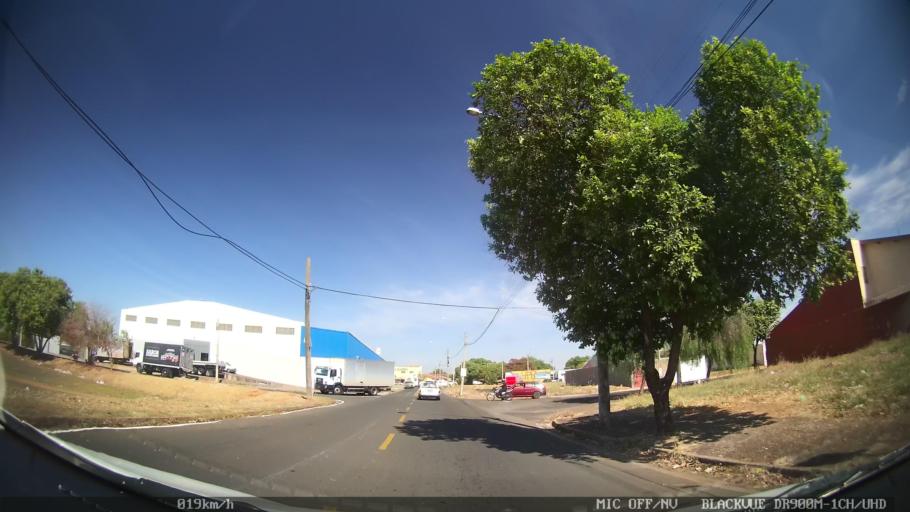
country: BR
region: Sao Paulo
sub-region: Sao Jose Do Rio Preto
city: Sao Jose do Rio Preto
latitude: -20.7729
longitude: -49.4145
